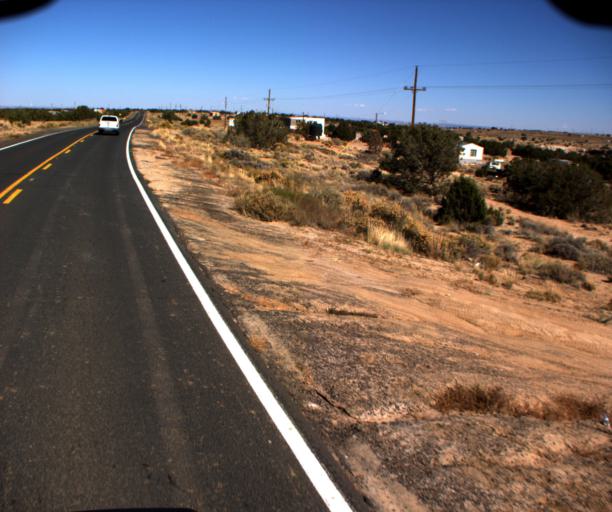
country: US
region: Arizona
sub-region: Navajo County
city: First Mesa
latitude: 35.8287
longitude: -110.5321
